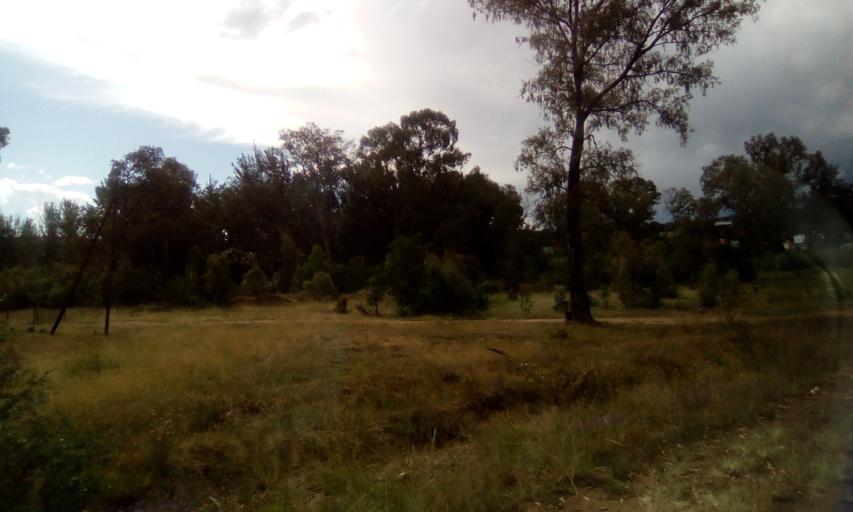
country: ZA
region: Orange Free State
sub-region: Thabo Mofutsanyana District Municipality
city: Ladybrand
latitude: -29.2006
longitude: 27.4648
